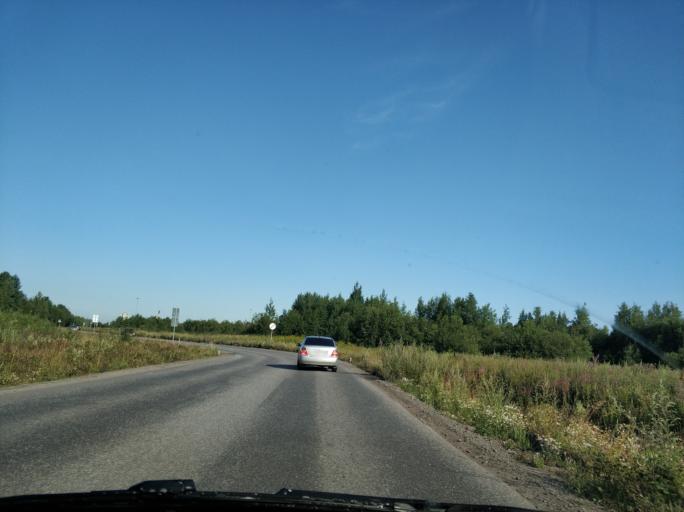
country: RU
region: St.-Petersburg
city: Grazhdanka
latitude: 60.0495
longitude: 30.4037
